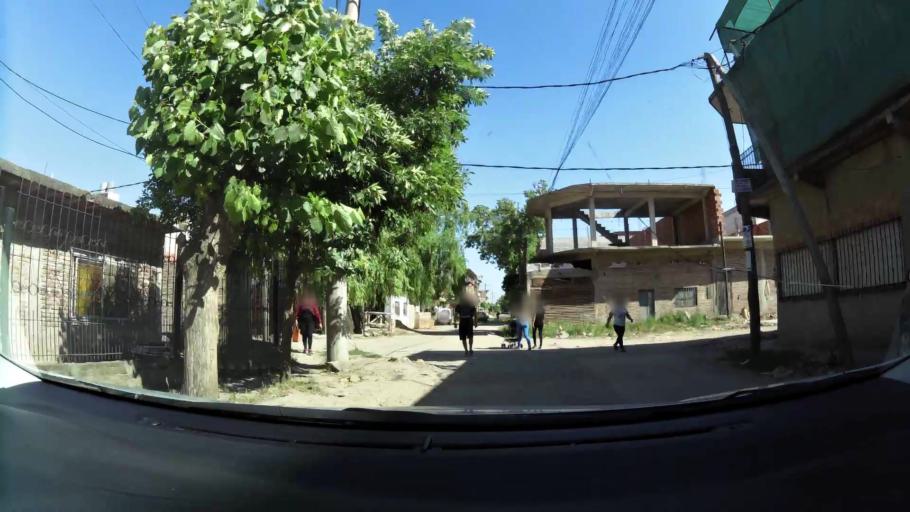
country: AR
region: Buenos Aires F.D.
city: Villa Lugano
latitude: -34.7097
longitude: -58.4777
